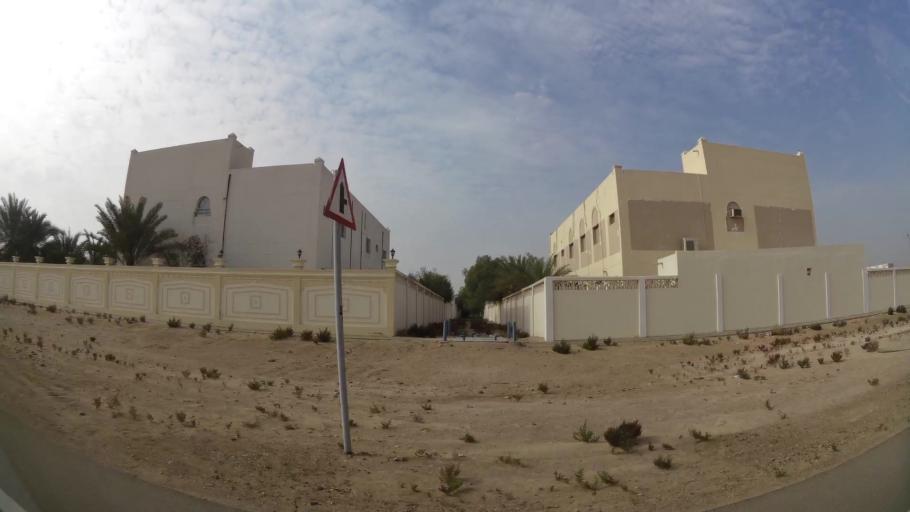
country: AE
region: Abu Dhabi
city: Abu Dhabi
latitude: 24.6633
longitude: 54.7610
